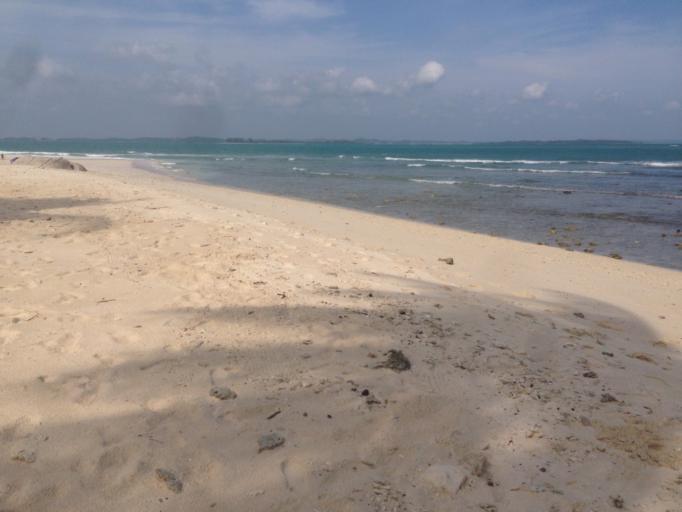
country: ID
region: Riau Islands
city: Kijang
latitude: 1.0530
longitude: 104.7078
